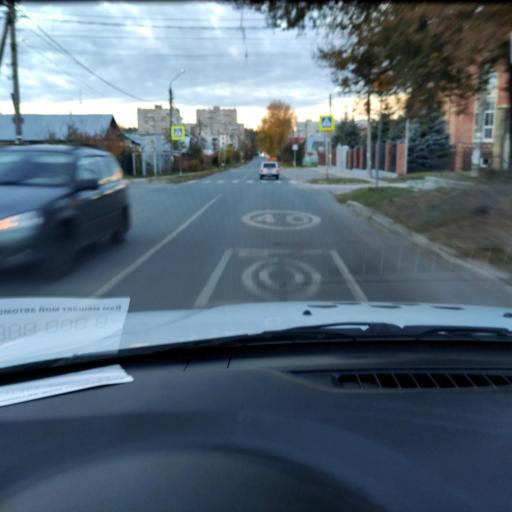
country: RU
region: Samara
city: Tol'yatti
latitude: 53.5321
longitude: 49.4023
